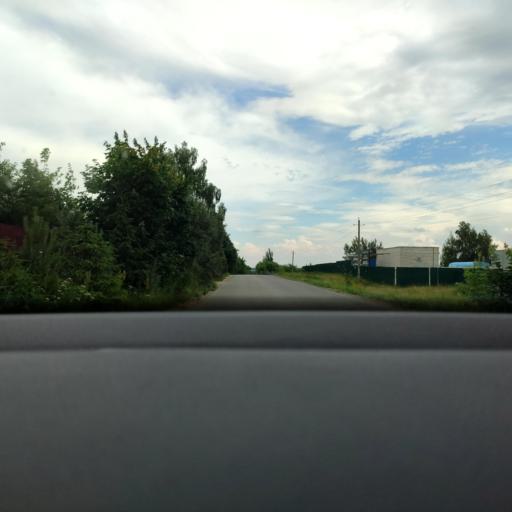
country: RU
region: Moskovskaya
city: Dedenevo
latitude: 56.2590
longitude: 37.5624
